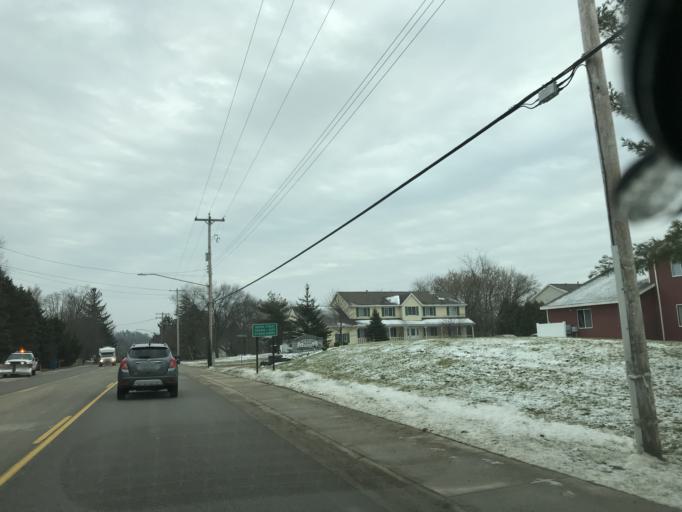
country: US
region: Michigan
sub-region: Kent County
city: Rockford
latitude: 43.1173
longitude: -85.5686
